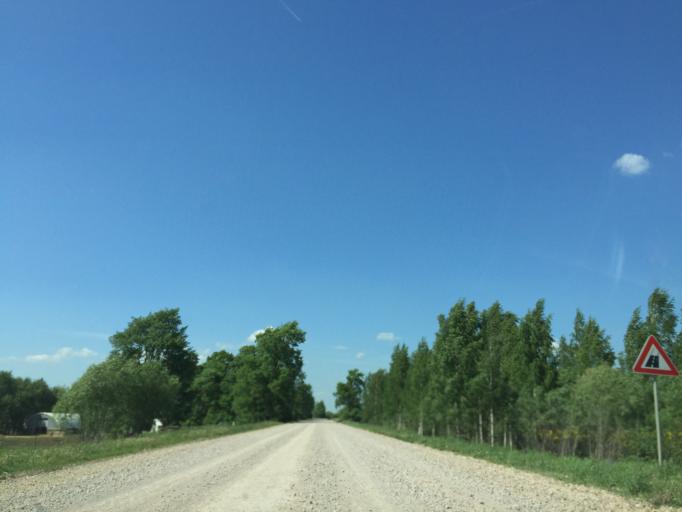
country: LV
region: Rundales
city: Pilsrundale
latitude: 56.5455
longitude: 23.9900
